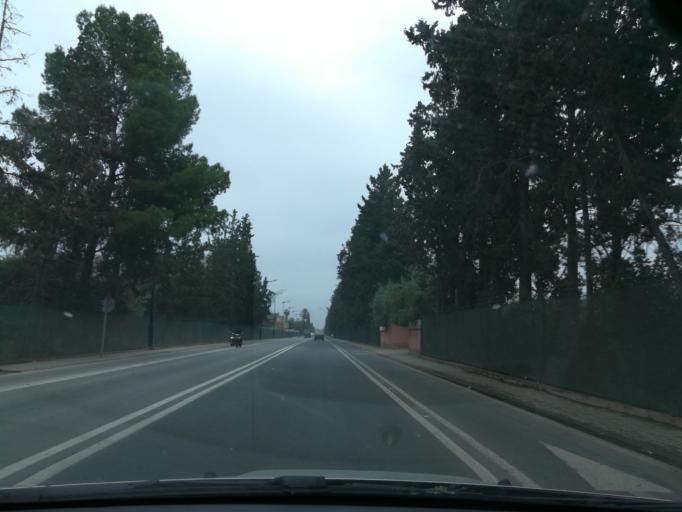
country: MA
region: Marrakech-Tensift-Al Haouz
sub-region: Marrakech
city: Marrakesh
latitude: 31.6013
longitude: -7.9845
